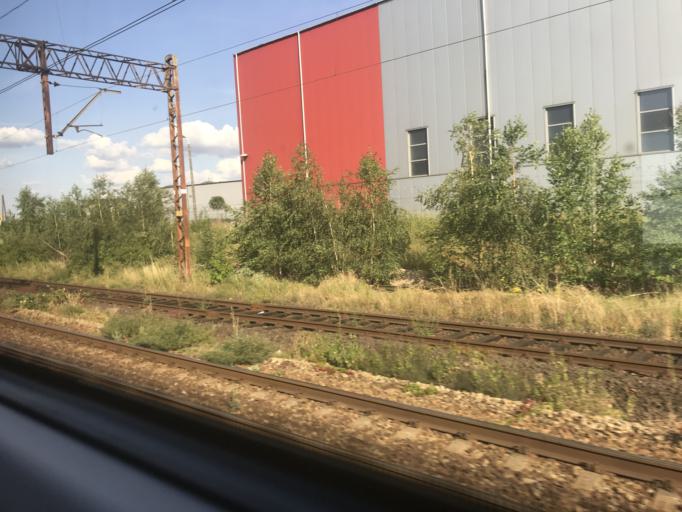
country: PL
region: West Pomeranian Voivodeship
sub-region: Szczecin
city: Szczecin
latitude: 53.3881
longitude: 14.6555
